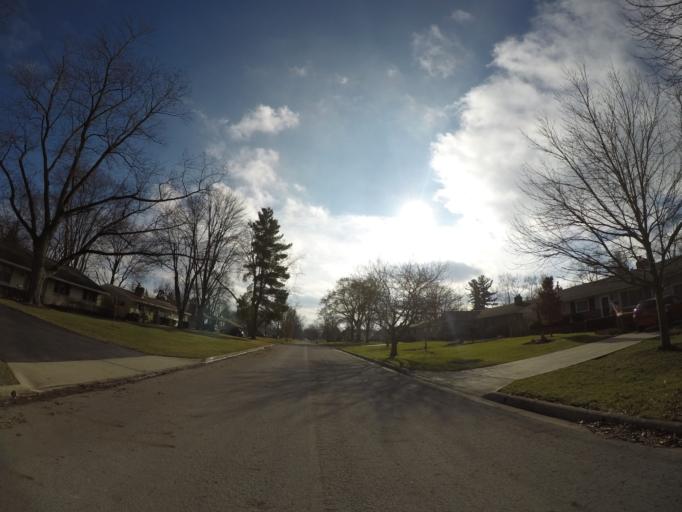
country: US
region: Ohio
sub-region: Franklin County
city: Upper Arlington
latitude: 40.0263
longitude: -83.0679
